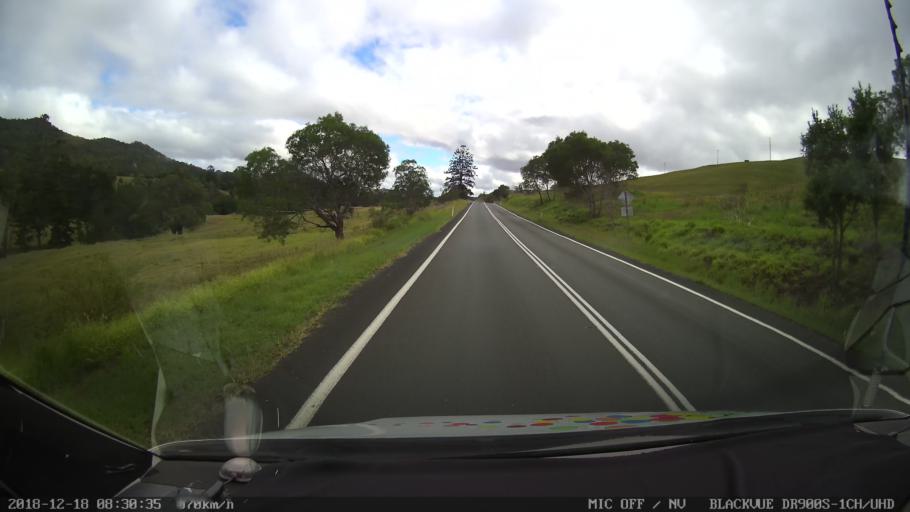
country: AU
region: New South Wales
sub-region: Kyogle
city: Kyogle
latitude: -28.3212
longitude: 152.7707
